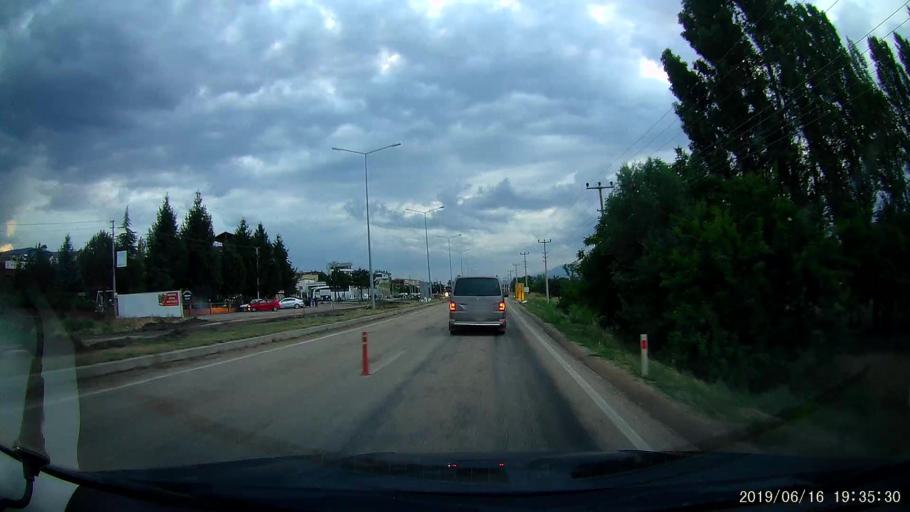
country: TR
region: Sivas
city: Susehri
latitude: 40.1705
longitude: 38.0925
